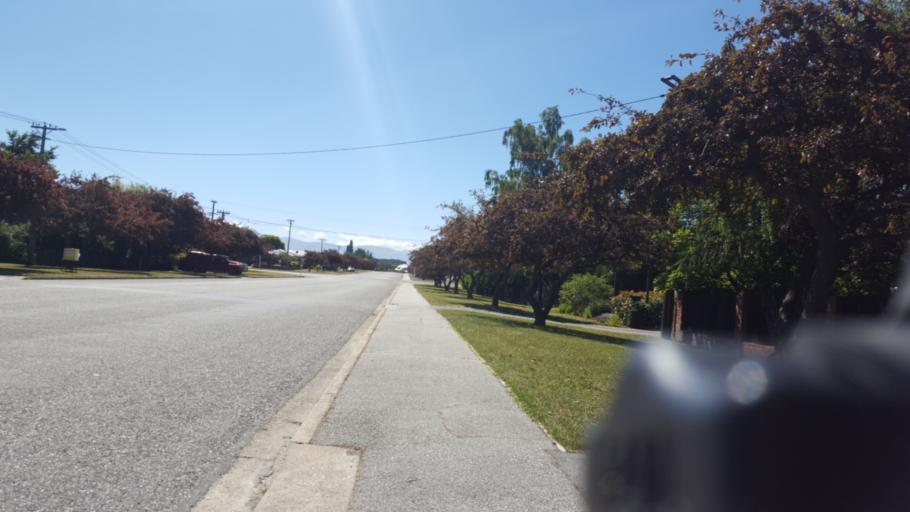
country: NZ
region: Otago
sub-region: Dunedin City
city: Dunedin
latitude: -45.1281
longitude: 170.0993
